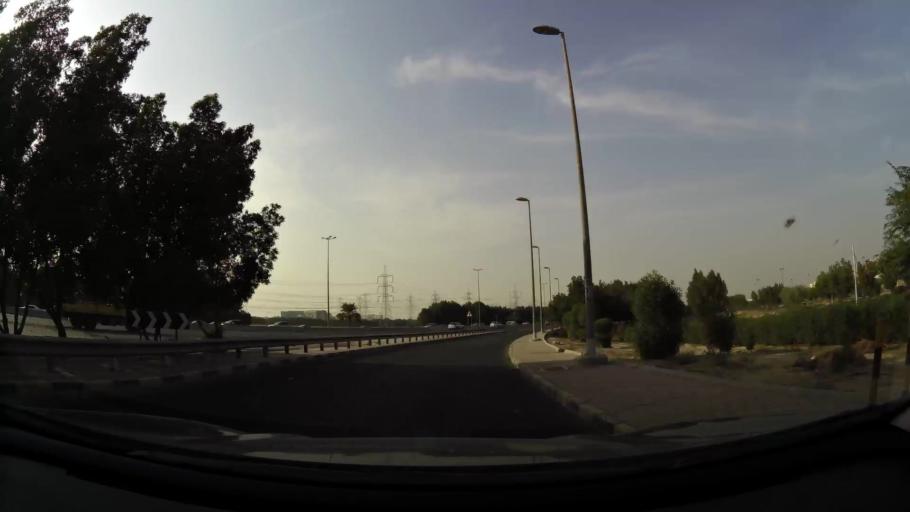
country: KW
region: Mubarak al Kabir
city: Mubarak al Kabir
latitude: 29.1932
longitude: 48.0640
